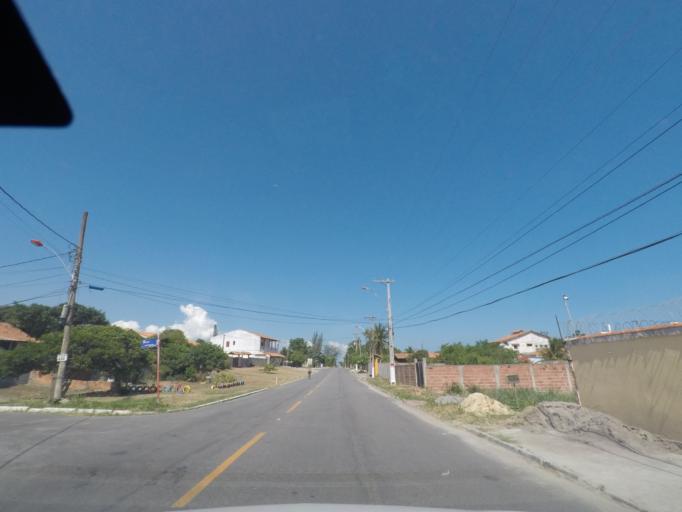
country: BR
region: Rio de Janeiro
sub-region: Marica
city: Marica
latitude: -22.9716
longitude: -42.9209
